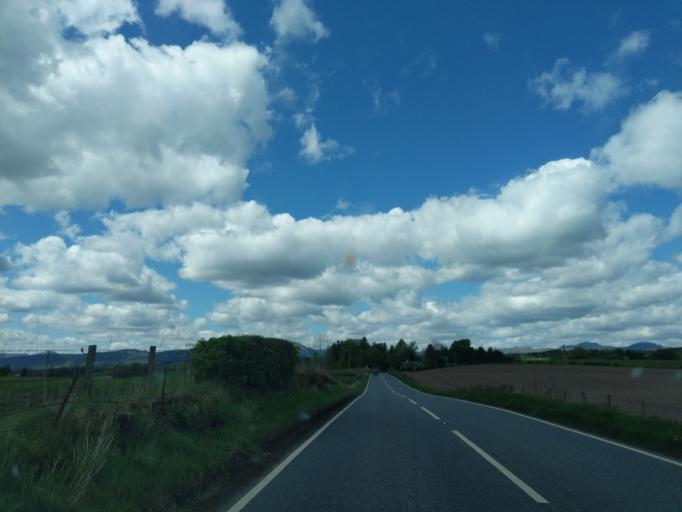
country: GB
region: Scotland
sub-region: Stirling
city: Doune
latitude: 56.1685
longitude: -4.1165
